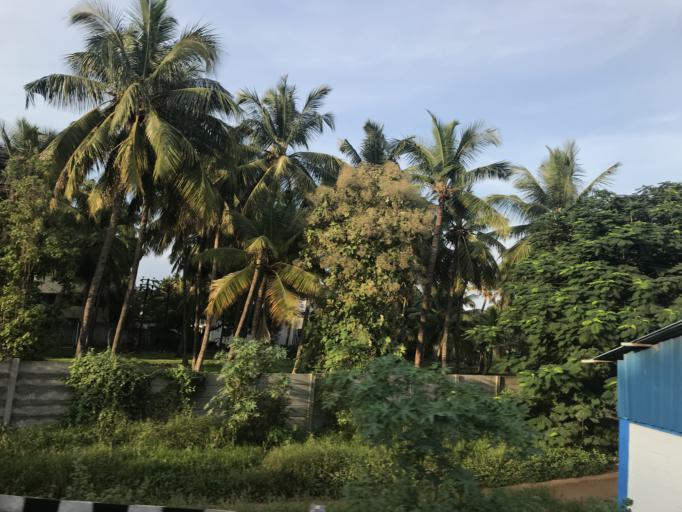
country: IN
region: Tamil Nadu
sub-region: Coimbatore
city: Coimbatore
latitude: 11.0307
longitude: 76.9680
